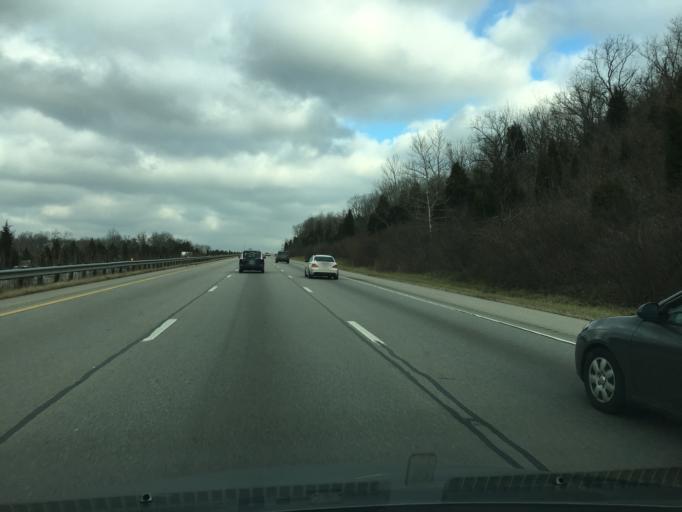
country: US
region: Ohio
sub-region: Hamilton County
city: Miamitown
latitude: 39.2182
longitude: -84.6691
